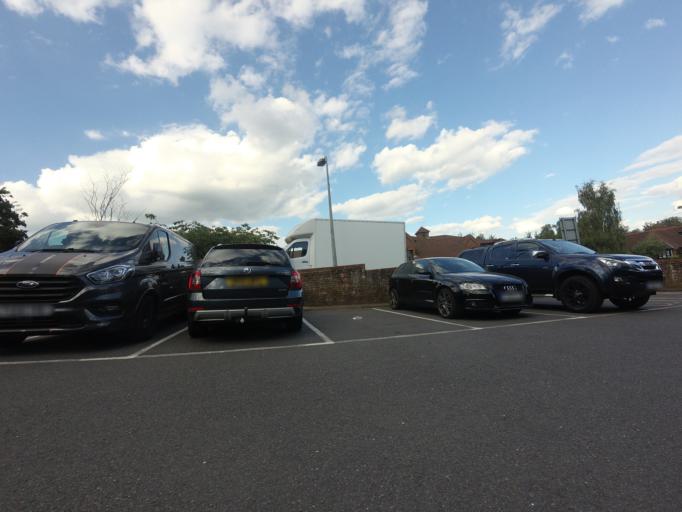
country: GB
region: England
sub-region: East Sussex
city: Horam
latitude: 50.9346
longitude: 0.2444
